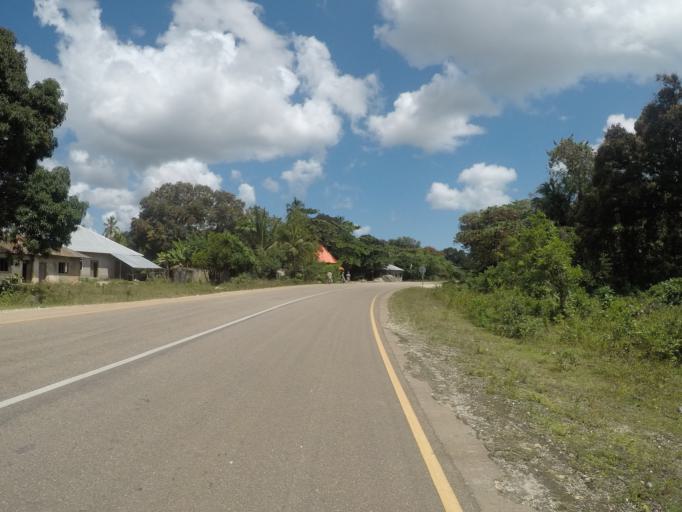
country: TZ
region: Zanzibar Central/South
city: Koani
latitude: -6.2342
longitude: 39.3597
